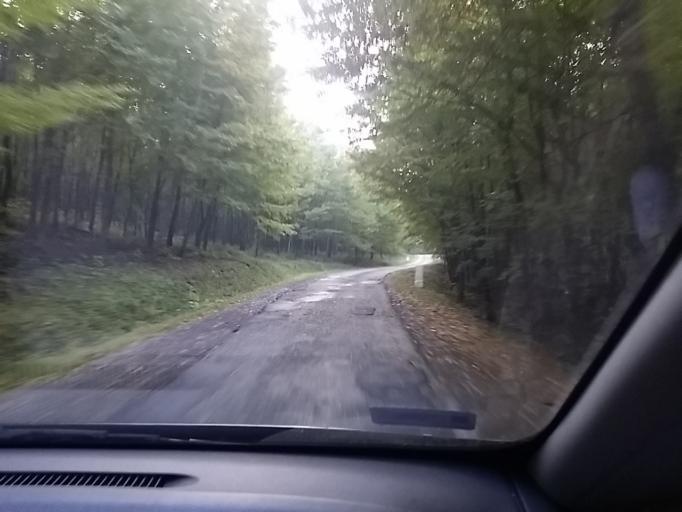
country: HU
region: Somogy
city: Kaposmero
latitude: 46.2599
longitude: 17.7495
